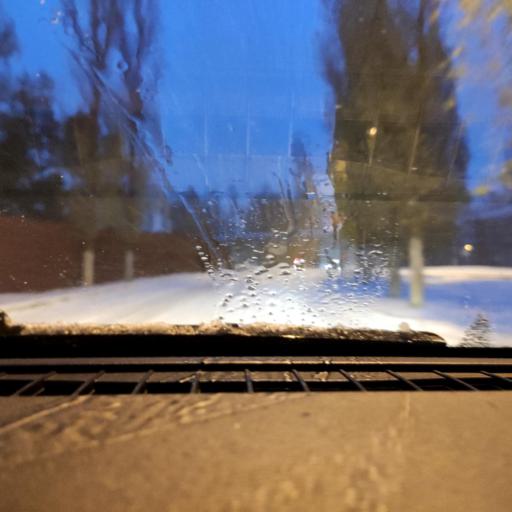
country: RU
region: Voronezj
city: Voronezh
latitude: 51.6301
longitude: 39.2286
